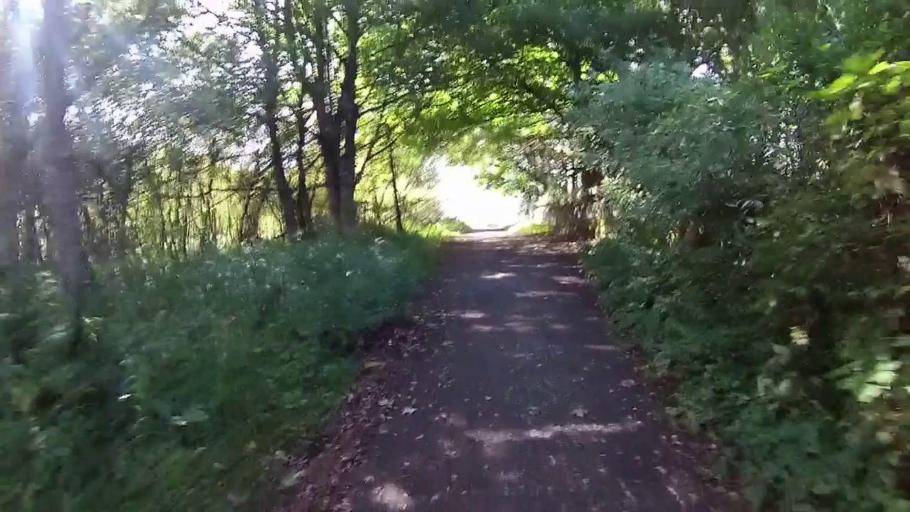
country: GB
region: Scotland
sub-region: Fife
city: Ballingry
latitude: 56.1791
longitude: -3.3381
